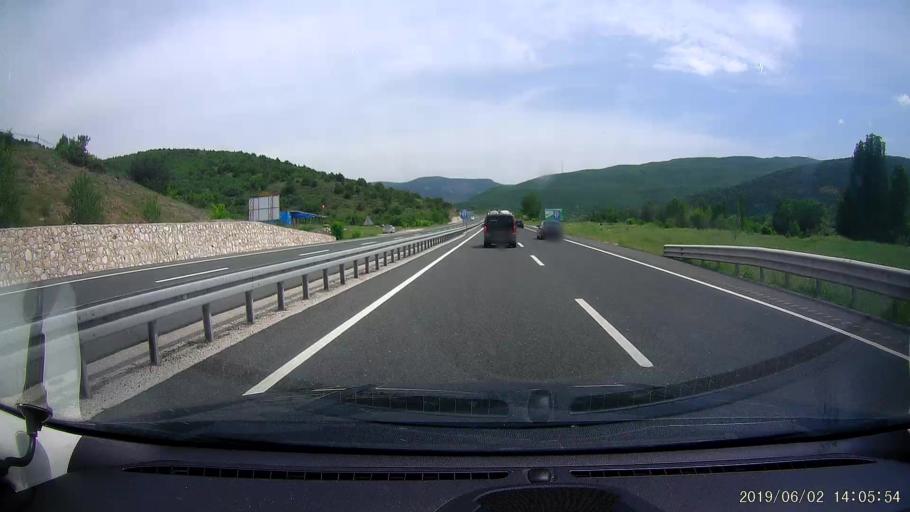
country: TR
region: Cankiri
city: Ilgaz
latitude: 40.8955
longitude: 33.6752
